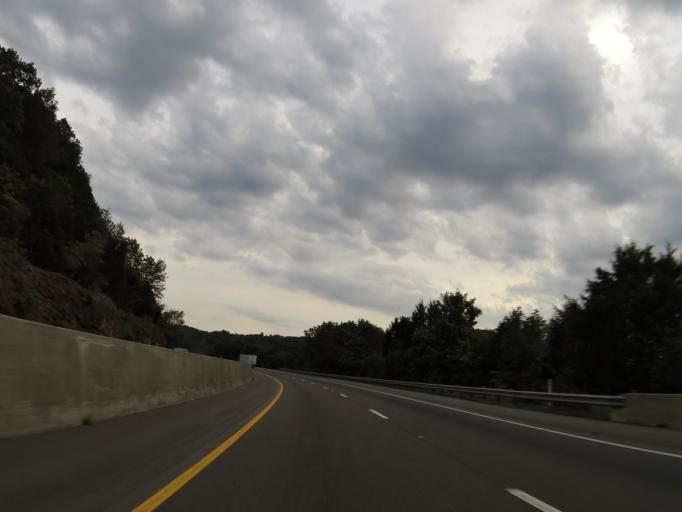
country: US
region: Tennessee
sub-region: Anderson County
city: Clinton
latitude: 36.0819
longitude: -84.0186
